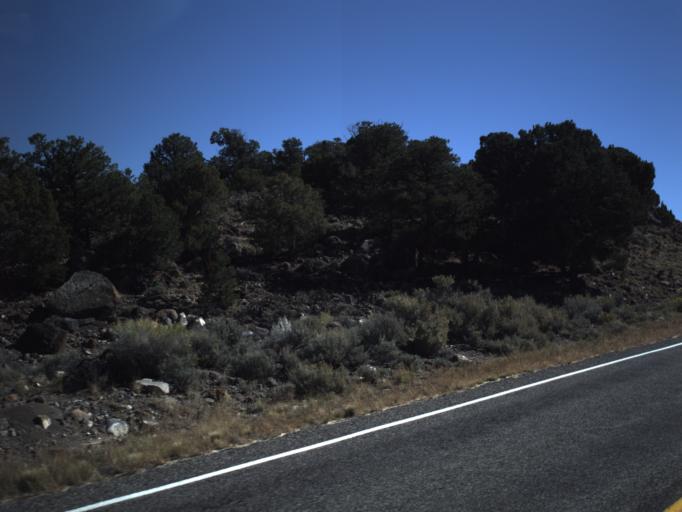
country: US
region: Utah
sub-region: Wayne County
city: Loa
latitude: 38.2365
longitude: -111.3712
